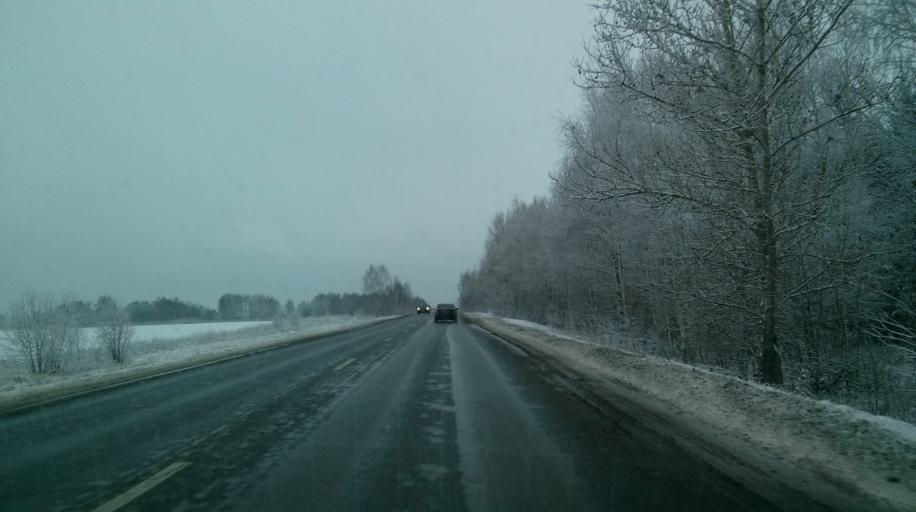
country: RU
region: Nizjnij Novgorod
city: Bogorodsk
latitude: 56.1087
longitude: 43.5891
